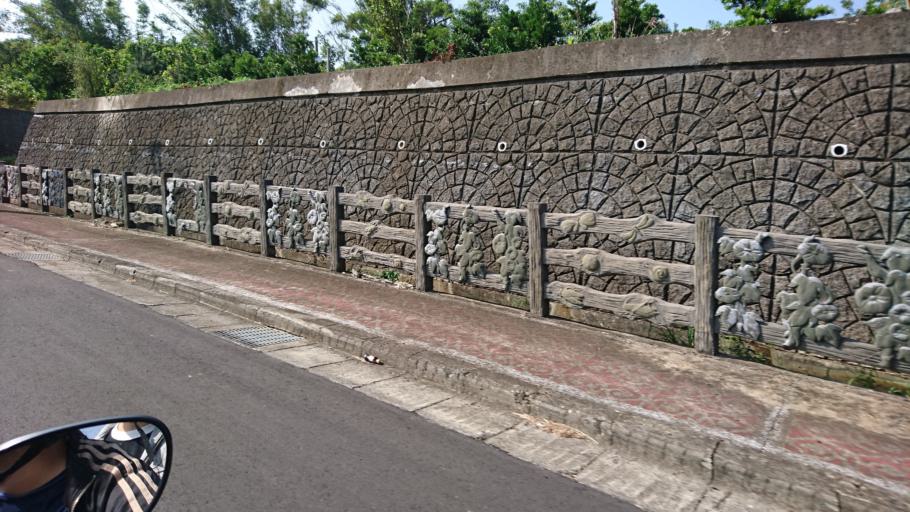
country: TW
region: Taiwan
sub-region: Hsinchu
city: Hsinchu
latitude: 24.7171
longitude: 120.9234
